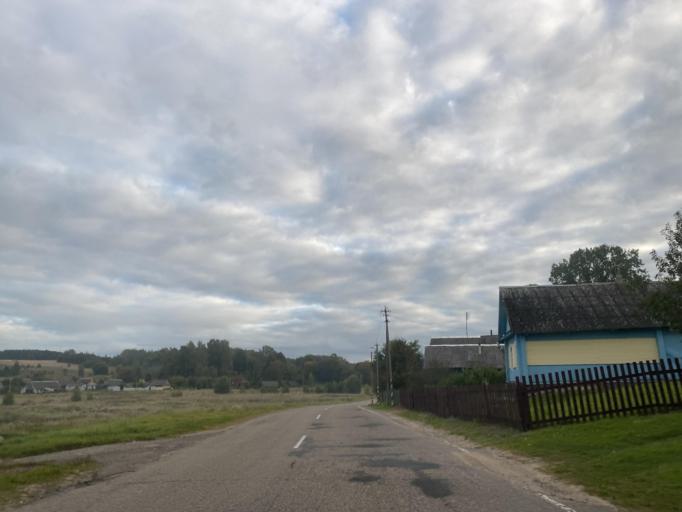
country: BY
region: Grodnenskaya
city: Kreva
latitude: 54.3071
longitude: 26.2791
